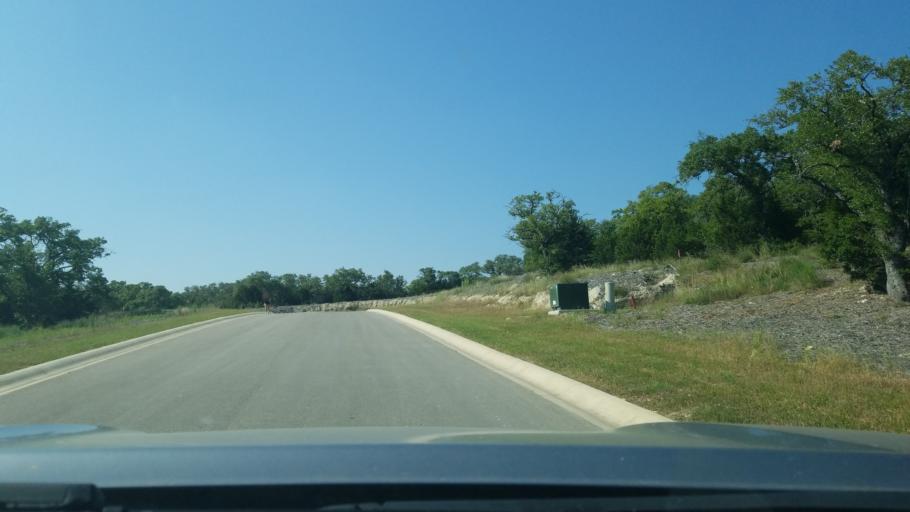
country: US
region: Texas
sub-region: Comal County
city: Bulverde
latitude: 29.7635
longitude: -98.4180
